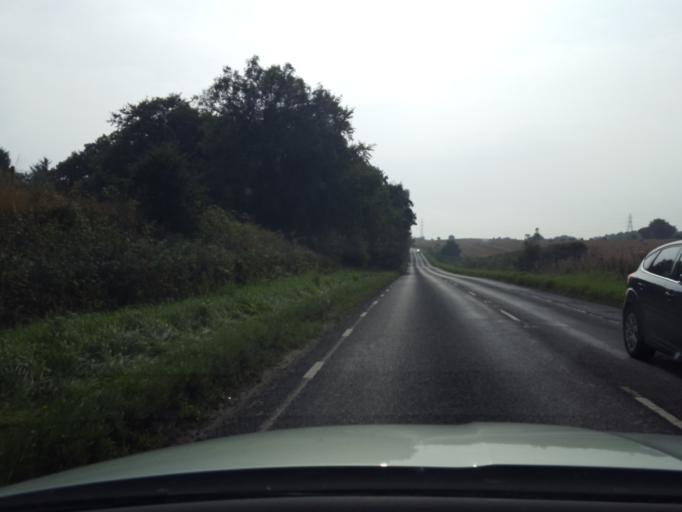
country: GB
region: Scotland
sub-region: Fife
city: Crossgates
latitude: 56.0642
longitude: -3.3789
